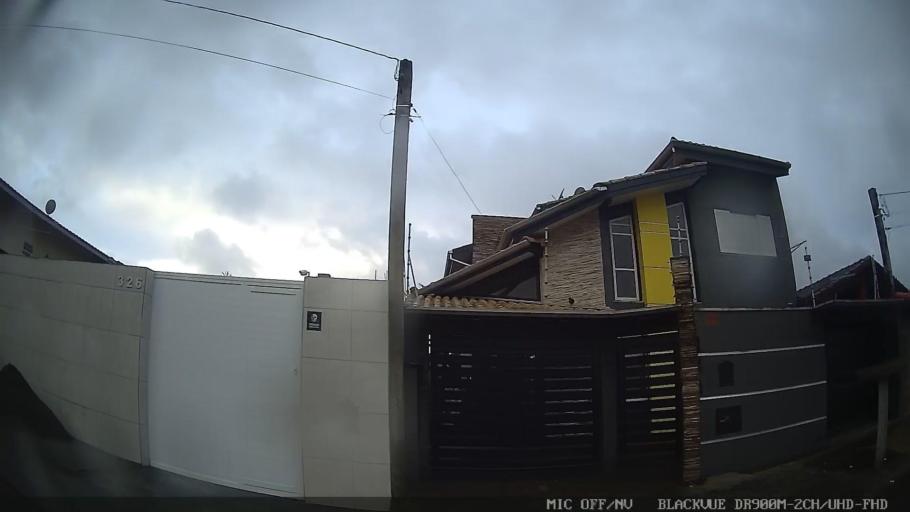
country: BR
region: Sao Paulo
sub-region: Itanhaem
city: Itanhaem
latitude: -24.1694
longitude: -46.7760
